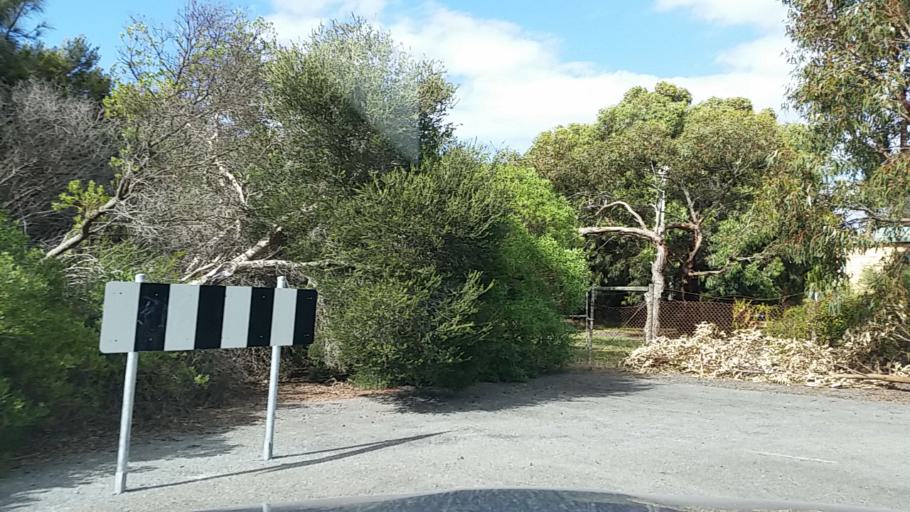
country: AU
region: South Australia
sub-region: Alexandrina
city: Port Elliot
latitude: -35.5298
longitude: 138.6880
